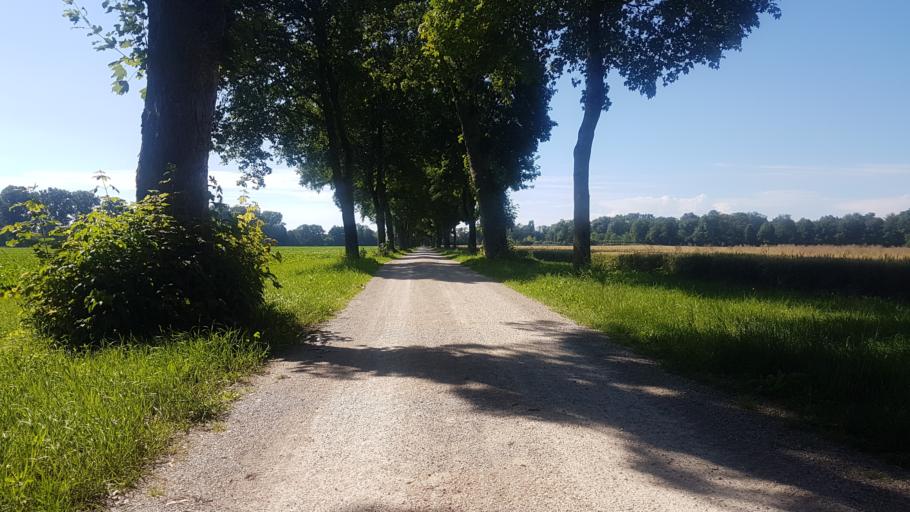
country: DE
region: Bavaria
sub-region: Upper Bavaria
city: Bergheim
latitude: 48.7332
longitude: 11.2680
